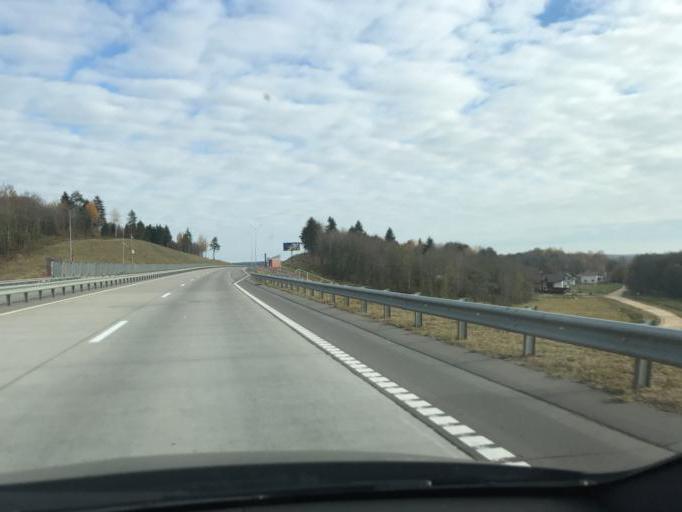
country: BY
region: Minsk
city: Pyatryshki
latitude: 54.0505
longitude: 27.1875
